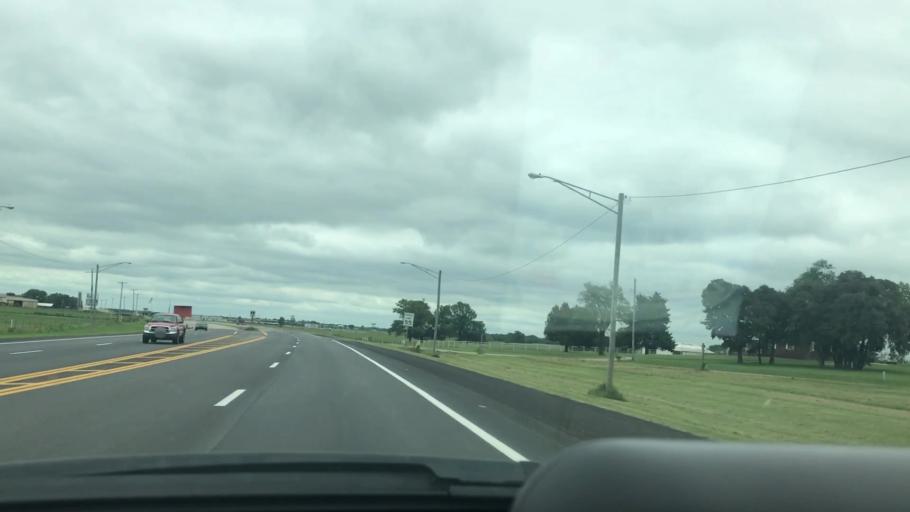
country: US
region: Oklahoma
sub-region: Craig County
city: Vinita
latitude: 36.5446
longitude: -95.2208
